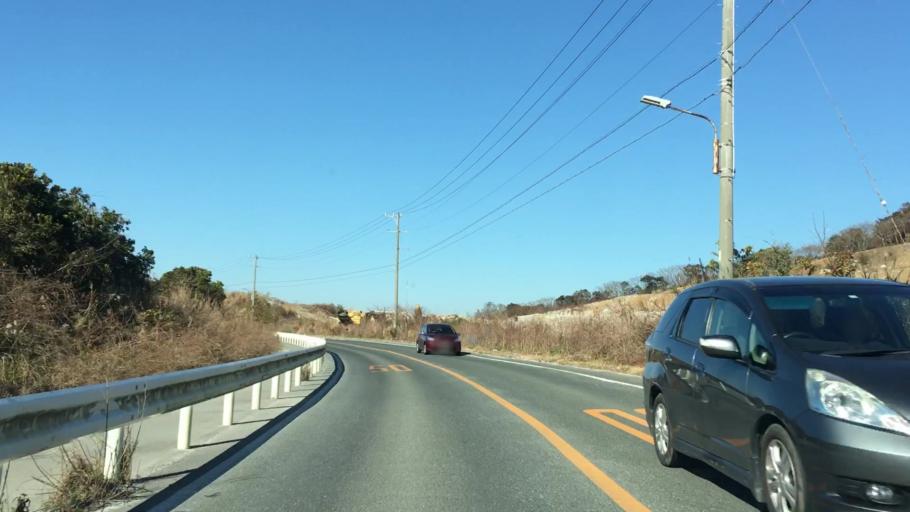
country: JP
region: Aichi
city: Tahara
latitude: 34.6827
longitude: 137.2510
